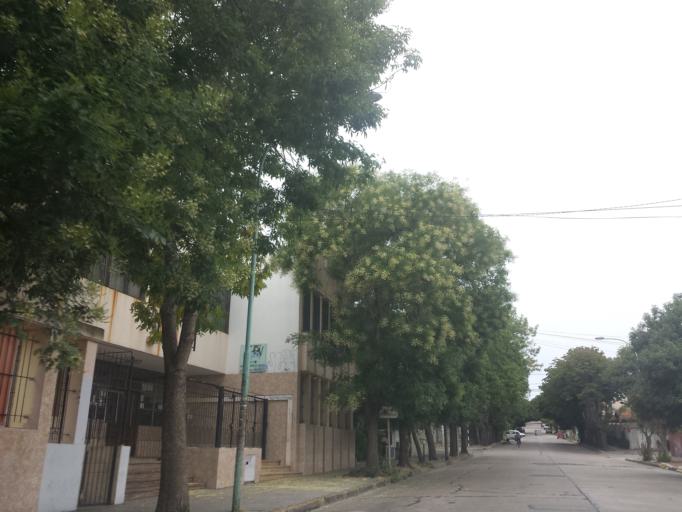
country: AR
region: Buenos Aires
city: Mar del Plata
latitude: -38.0161
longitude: -57.5386
